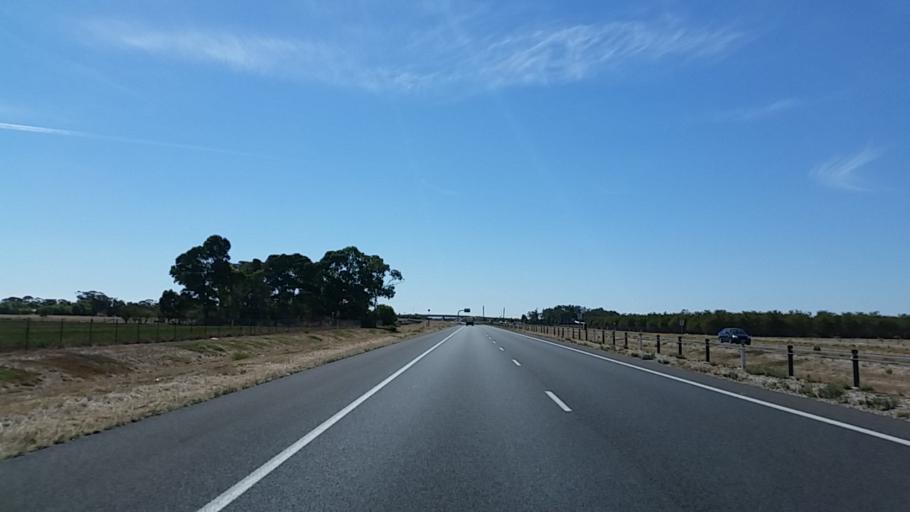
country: AU
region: South Australia
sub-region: Playford
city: Angle Vale
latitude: -34.6446
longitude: 138.6663
